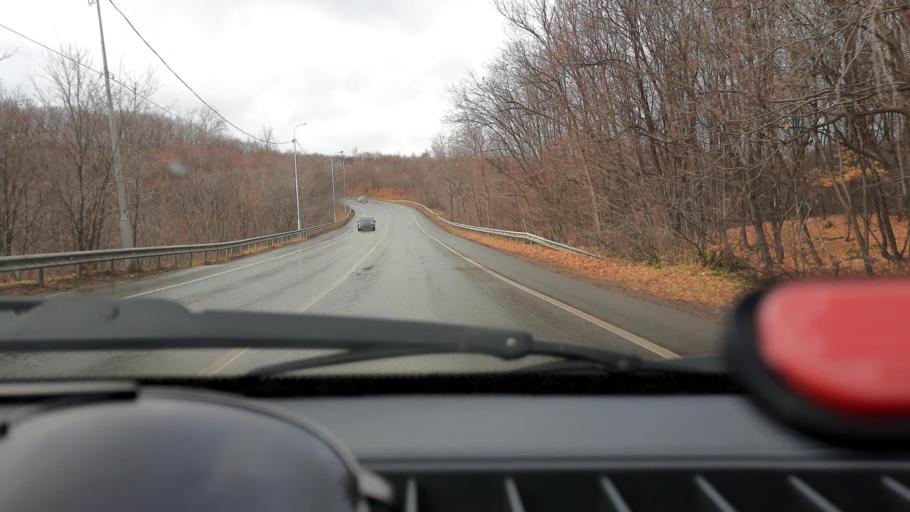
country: RU
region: Bashkortostan
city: Ufa
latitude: 54.8809
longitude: 56.0601
